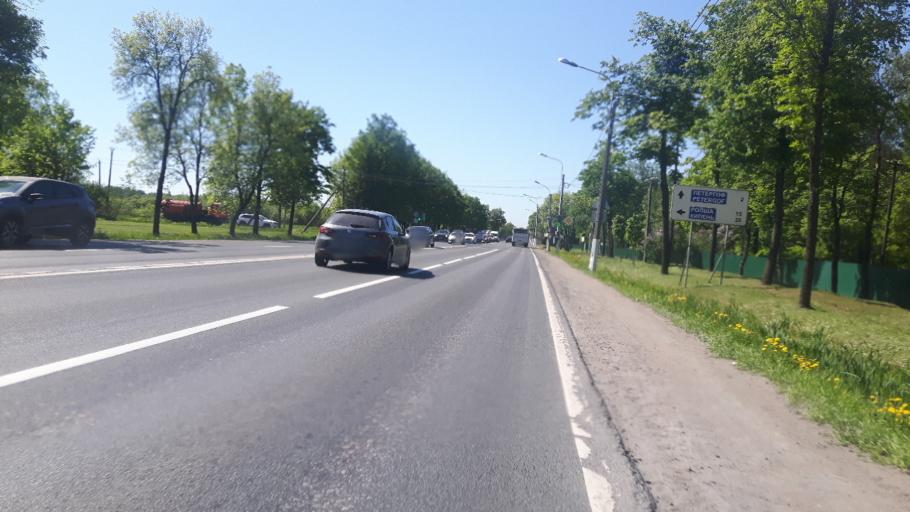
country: RU
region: Leningrad
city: Ol'gino
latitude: 59.8723
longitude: 29.9636
